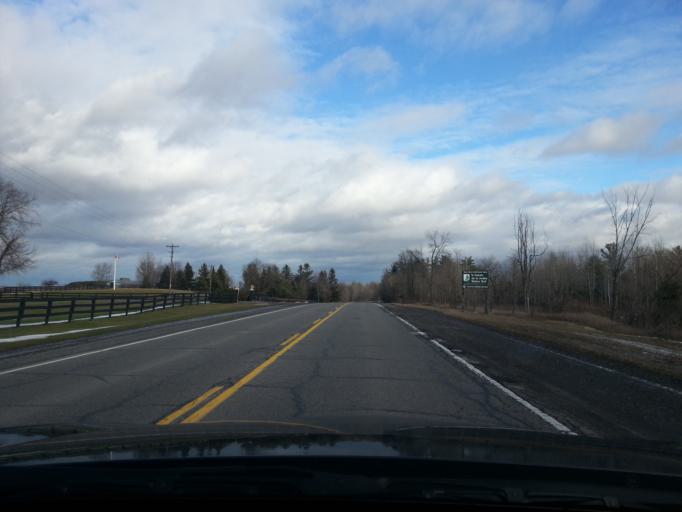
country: CA
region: Ontario
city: Prescott
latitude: 45.0456
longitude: -75.5774
